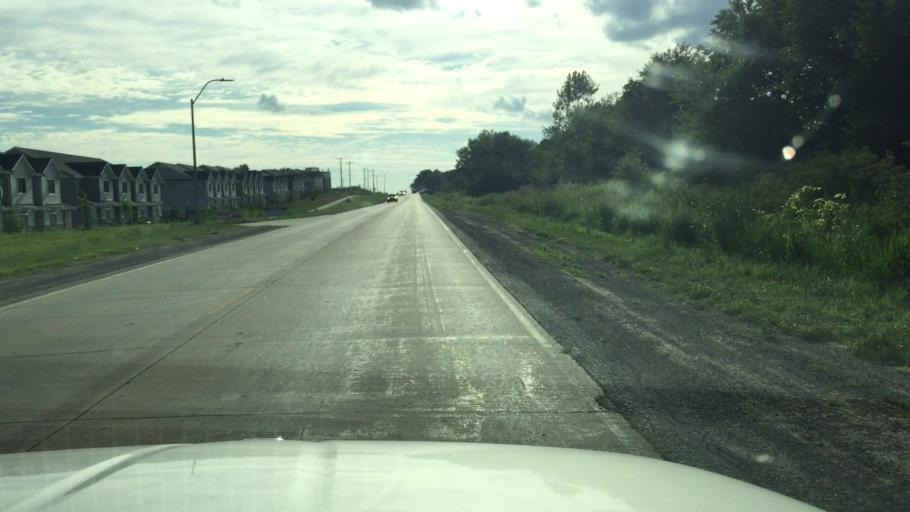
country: US
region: Iowa
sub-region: Johnson County
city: Iowa City
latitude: 41.6711
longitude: -91.4678
